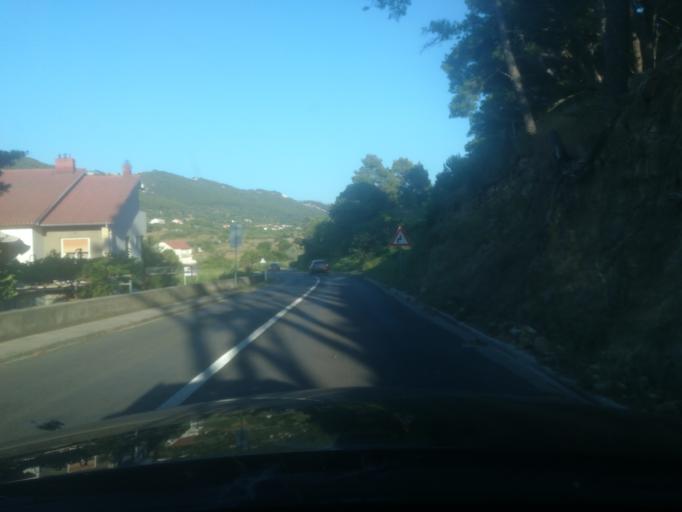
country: HR
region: Primorsko-Goranska
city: Banjol
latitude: 44.7582
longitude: 14.7713
